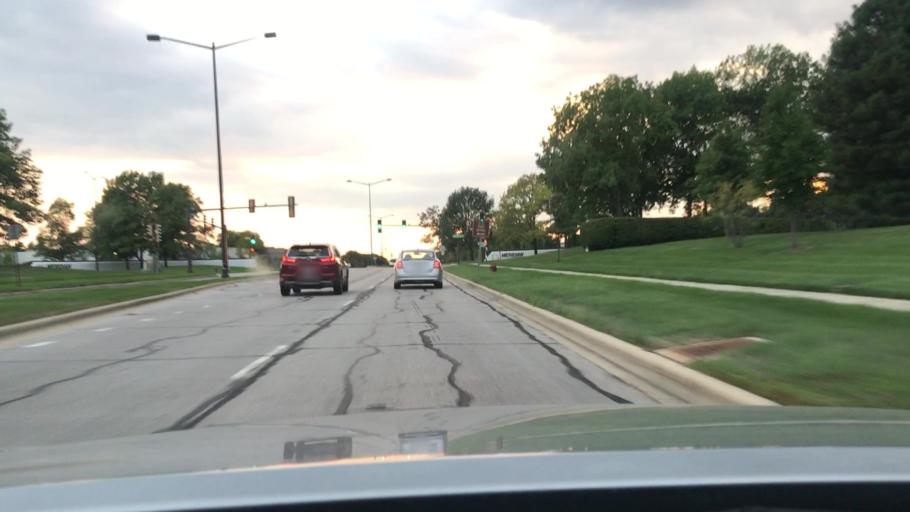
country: US
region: Illinois
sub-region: DuPage County
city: Warrenville
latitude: 41.7690
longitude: -88.2194
